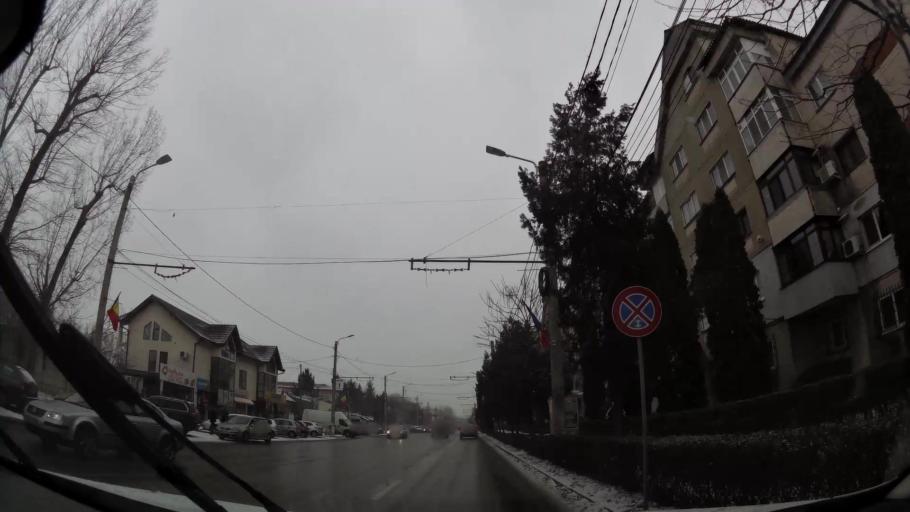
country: RO
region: Dambovita
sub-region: Municipiul Targoviste
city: Targoviste
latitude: 44.9185
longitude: 25.4626
